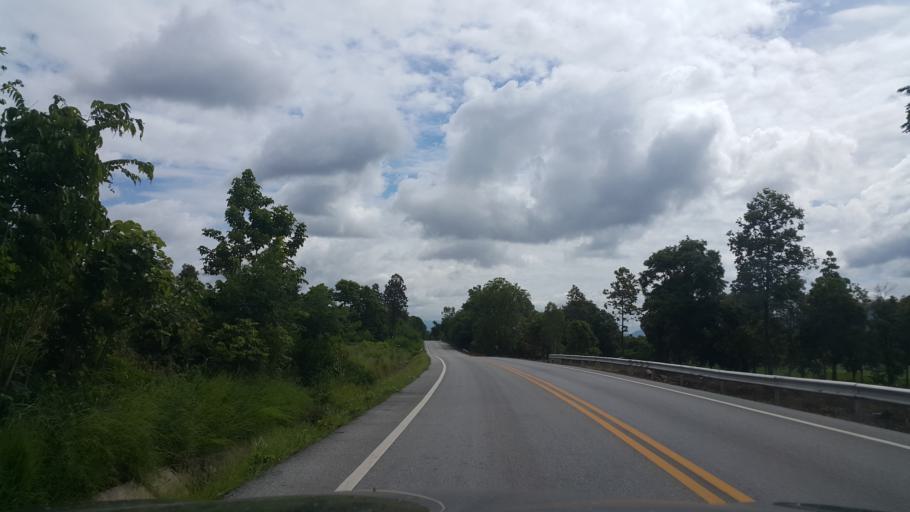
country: TH
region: Uttaradit
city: Thong Saen Khan
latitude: 17.3846
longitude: 100.2884
